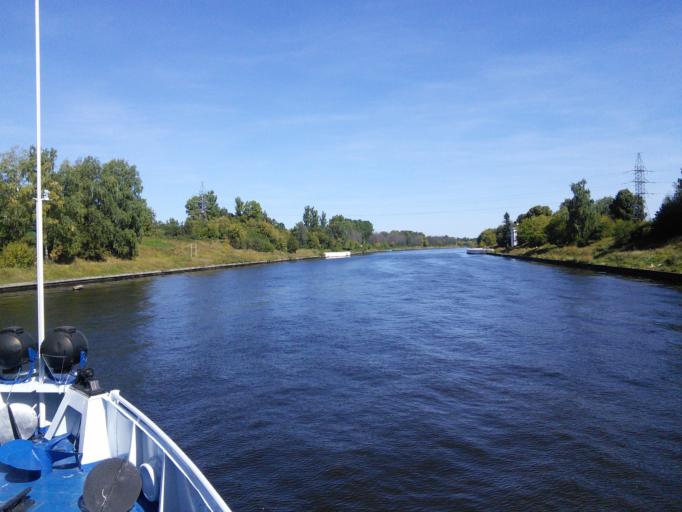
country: RU
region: Moskovskaya
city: Dolgoprudnyy
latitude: 55.9473
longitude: 37.4795
